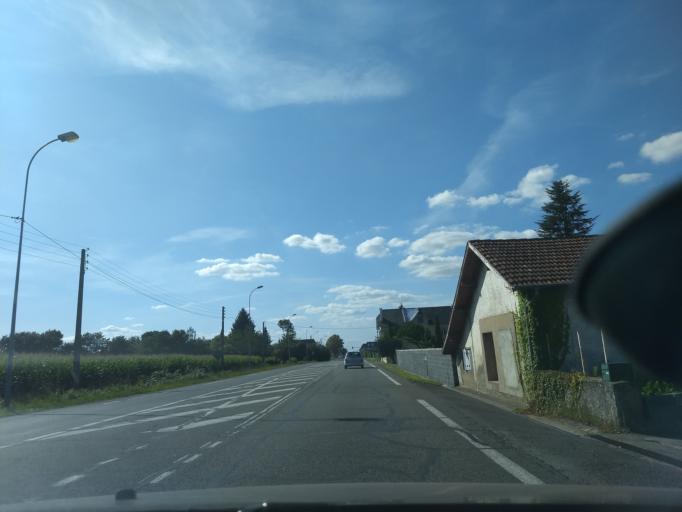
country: FR
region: Aquitaine
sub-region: Departement des Pyrenees-Atlantiques
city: Ousse
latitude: 43.2882
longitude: -0.2665
